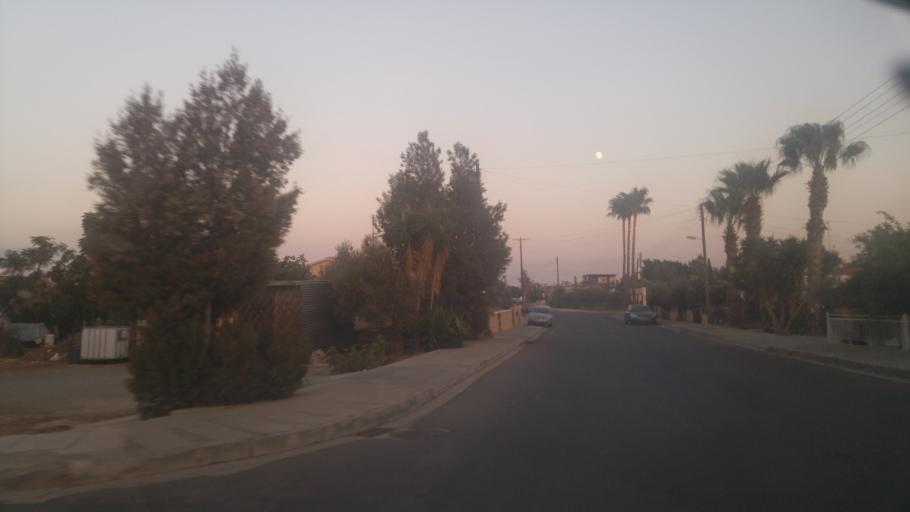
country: CY
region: Larnaka
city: Kolossi
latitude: 34.6610
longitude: 32.9582
